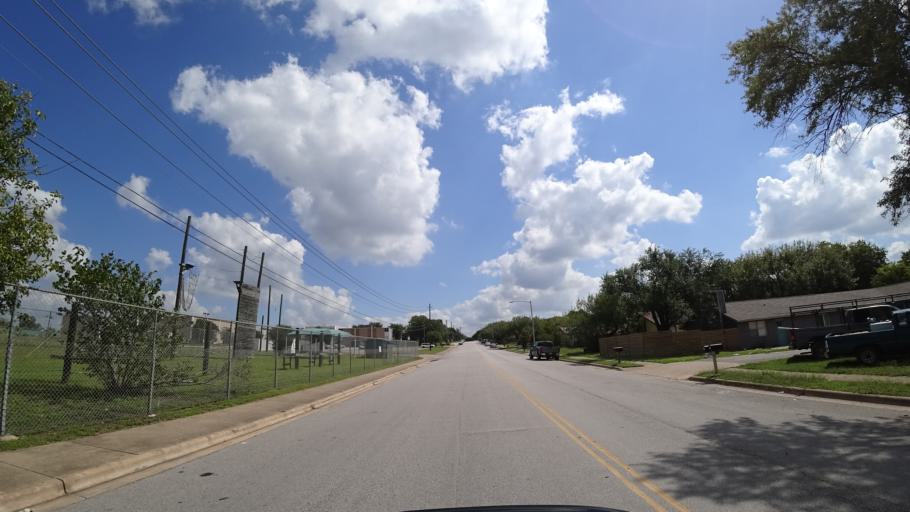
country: US
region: Texas
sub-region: Travis County
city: Onion Creek
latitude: 30.1943
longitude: -97.7892
